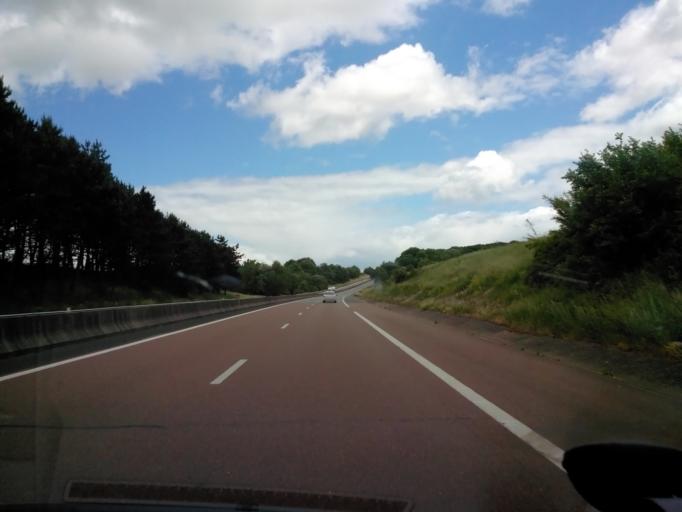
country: FR
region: Champagne-Ardenne
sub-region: Departement de la Haute-Marne
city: Saulxures
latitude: 48.0787
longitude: 5.6100
